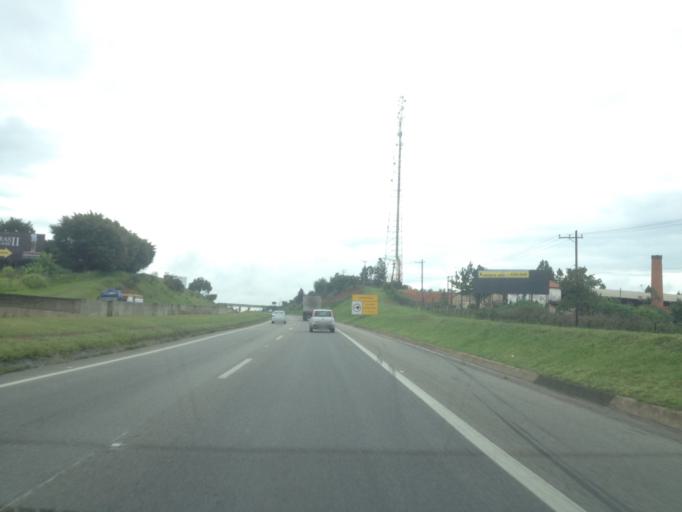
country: BR
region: Sao Paulo
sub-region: Itu
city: Itu
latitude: -23.3829
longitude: -47.3277
